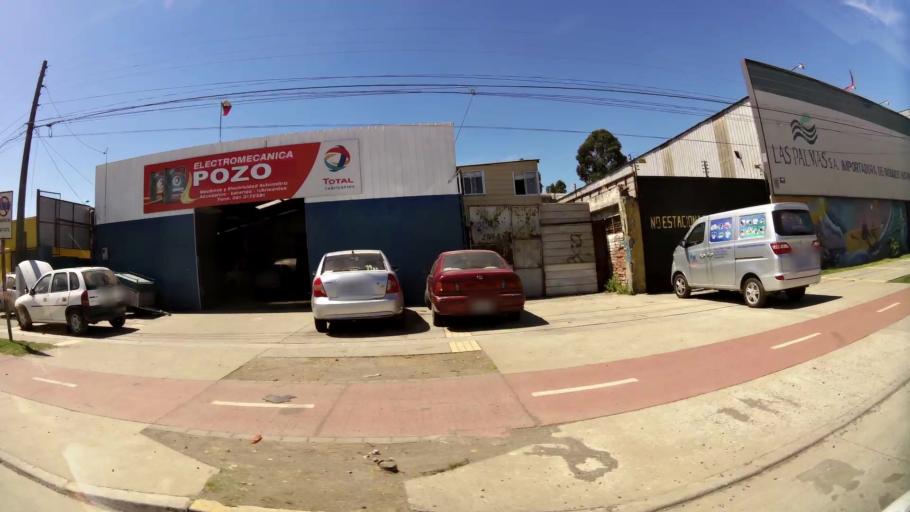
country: CL
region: Biobio
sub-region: Provincia de Concepcion
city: Talcahuano
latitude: -36.7359
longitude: -73.1040
